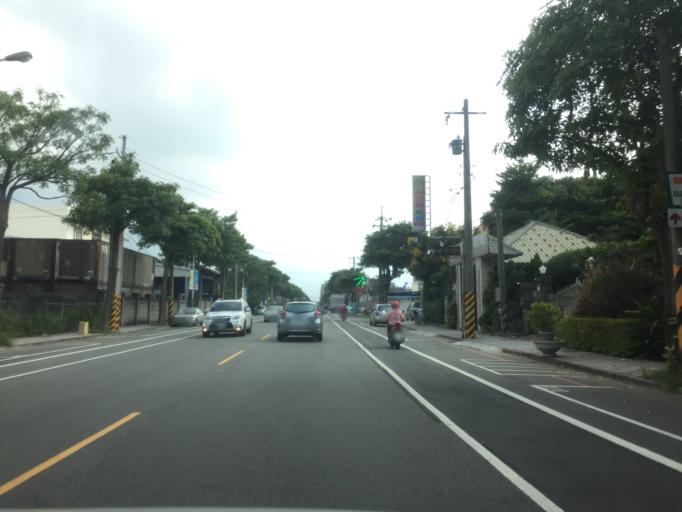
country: TW
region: Taiwan
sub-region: Taoyuan
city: Taoyuan
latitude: 24.9725
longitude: 121.3069
